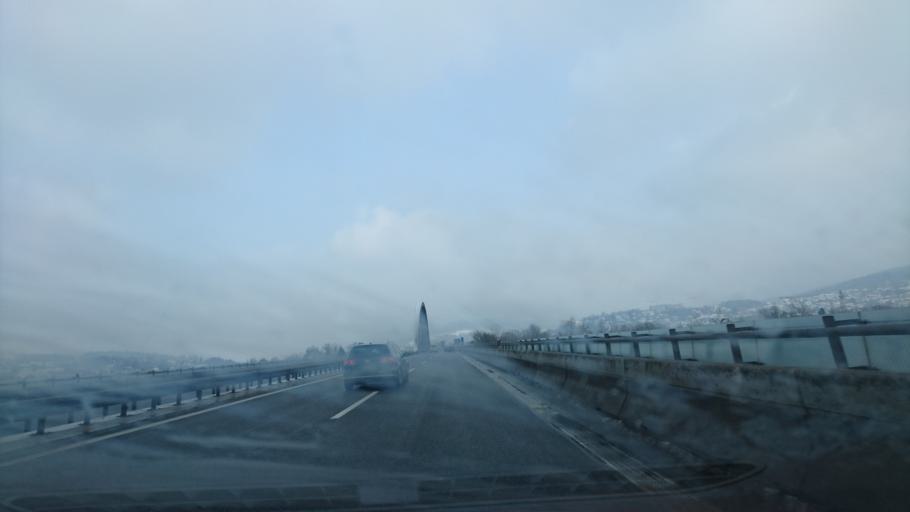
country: DE
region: Bavaria
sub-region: Lower Bavaria
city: Deggendorf
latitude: 48.8269
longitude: 12.9474
